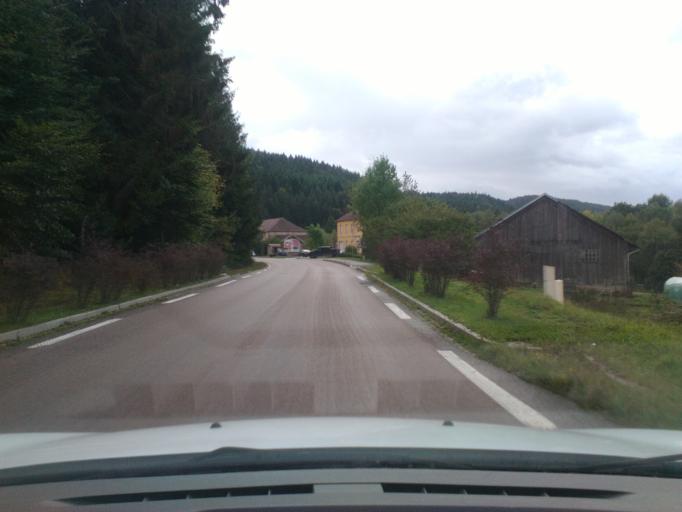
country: FR
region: Lorraine
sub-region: Departement des Vosges
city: Bruyeres
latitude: 48.2563
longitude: 6.7918
